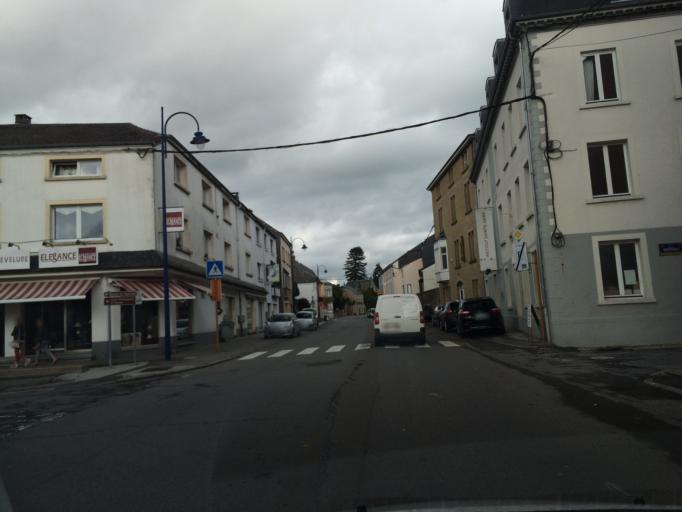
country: BE
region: Wallonia
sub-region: Province du Luxembourg
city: Florenville
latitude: 49.6984
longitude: 5.3122
